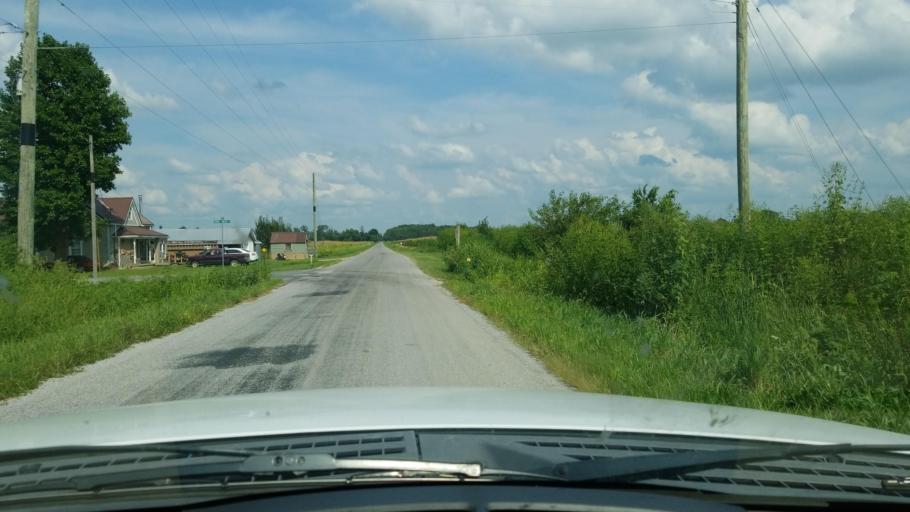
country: US
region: Illinois
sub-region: Saline County
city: Eldorado
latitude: 37.8630
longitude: -88.5038
